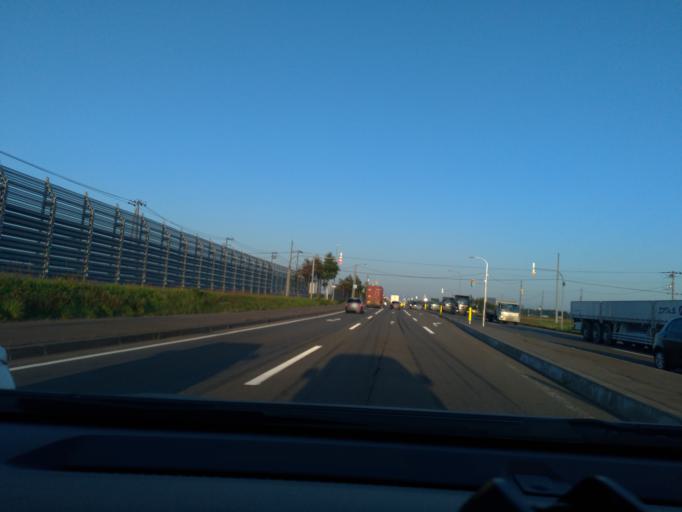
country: JP
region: Hokkaido
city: Tobetsu
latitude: 43.1791
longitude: 141.4617
